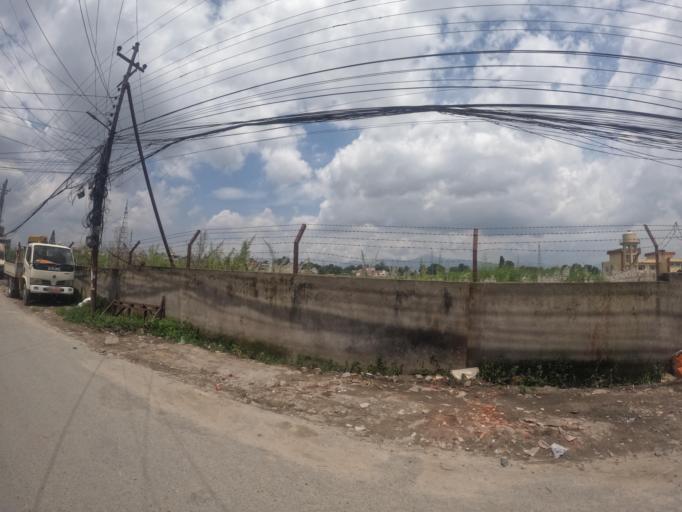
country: NP
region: Central Region
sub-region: Bagmati Zone
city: Bhaktapur
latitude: 27.6767
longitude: 85.3777
